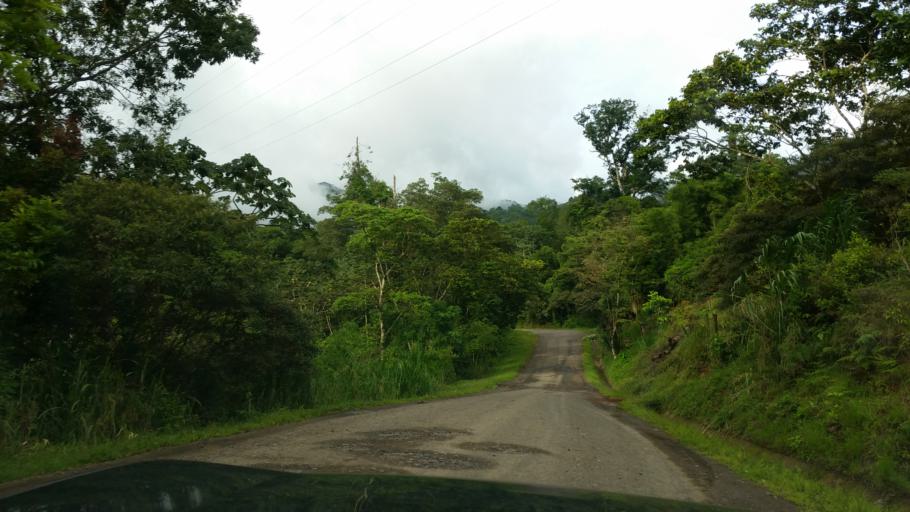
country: NI
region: Jinotega
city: Jinotega
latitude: 13.2625
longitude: -85.7336
